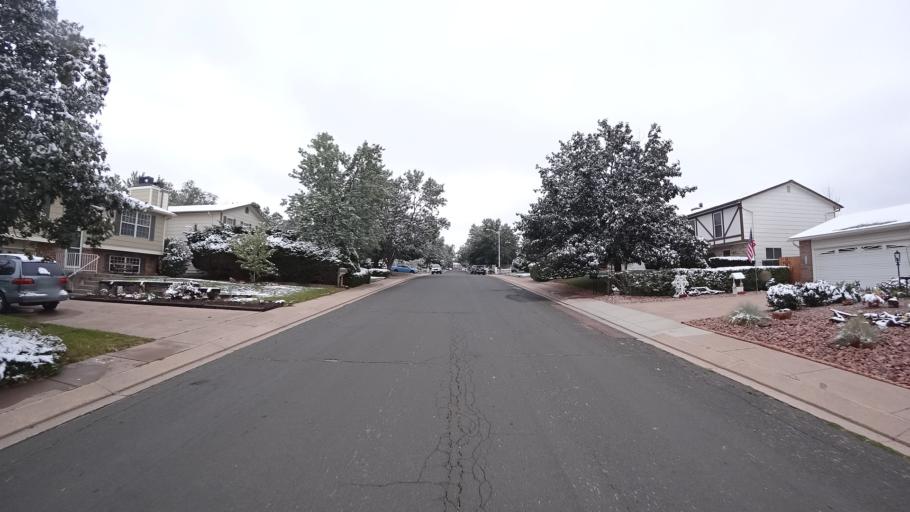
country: US
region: Colorado
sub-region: El Paso County
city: Cimarron Hills
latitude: 38.9289
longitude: -104.7667
